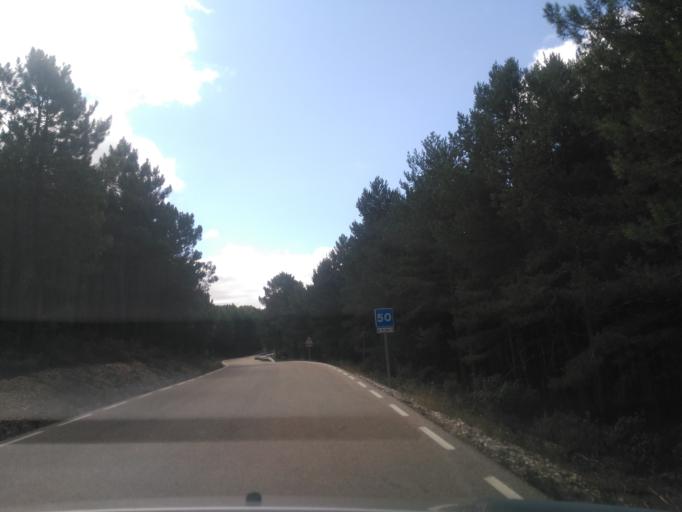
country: ES
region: Castille and Leon
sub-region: Provincia de Soria
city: Espejon
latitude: 41.8438
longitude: -3.2379
